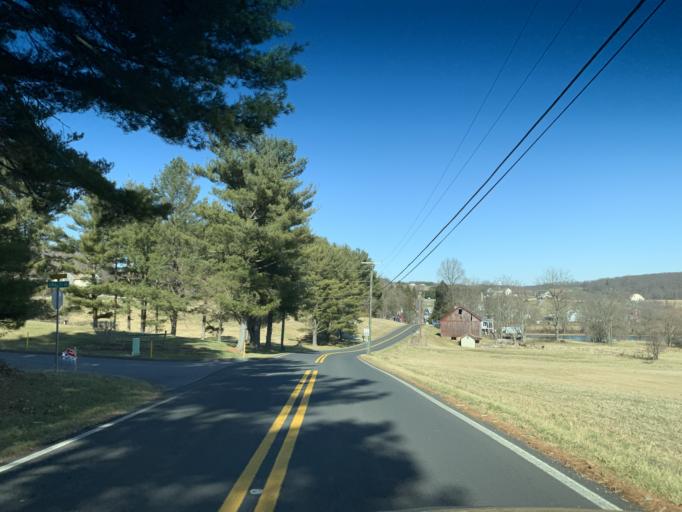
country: US
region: Maryland
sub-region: Carroll County
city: Manchester
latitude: 39.6159
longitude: -76.8982
